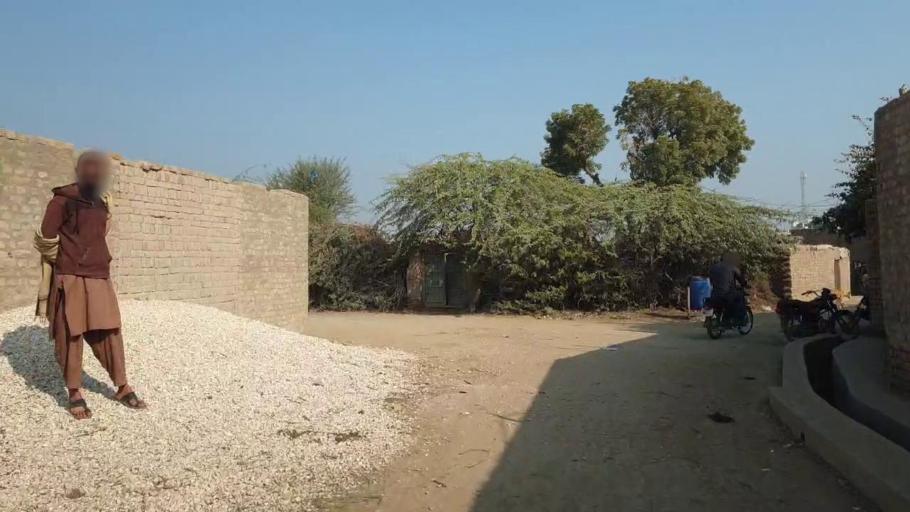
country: PK
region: Sindh
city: Matiari
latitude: 25.6760
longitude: 68.5005
